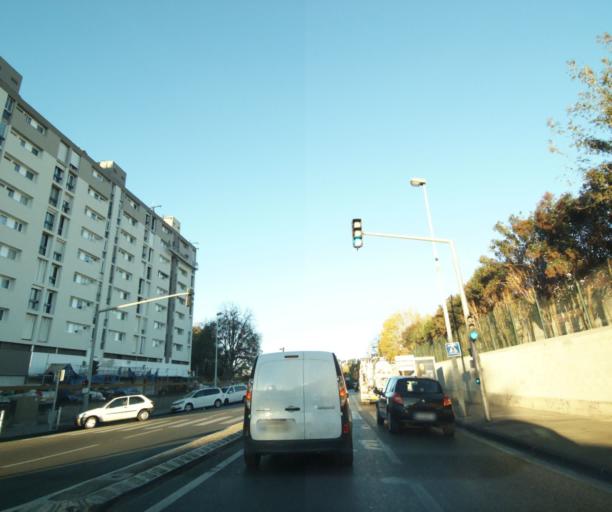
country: FR
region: Provence-Alpes-Cote d'Azur
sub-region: Departement des Bouches-du-Rhone
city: Marseille 13
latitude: 43.3287
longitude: 5.4326
